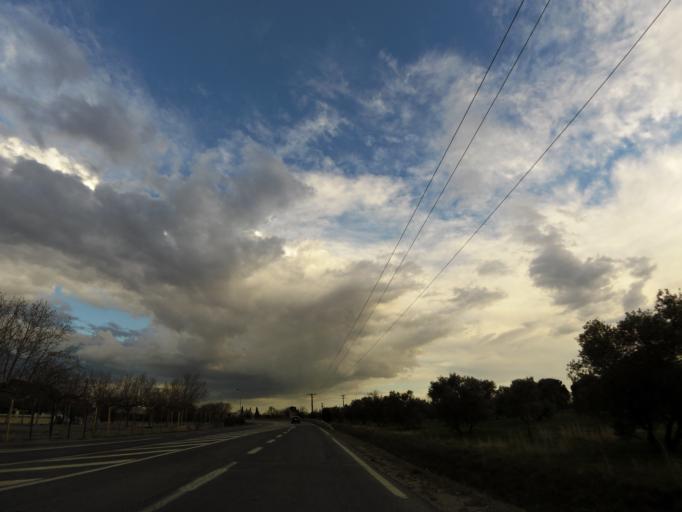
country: FR
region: Languedoc-Roussillon
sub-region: Departement du Gard
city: Codognan
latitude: 43.7277
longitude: 4.2408
